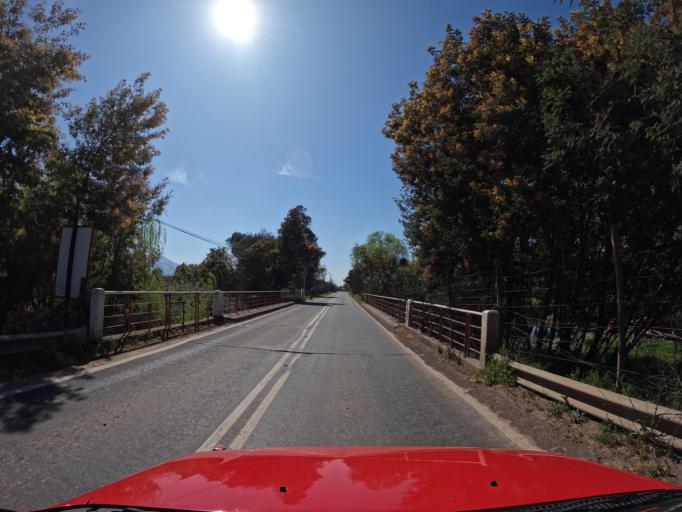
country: CL
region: Maule
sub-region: Provincia de Curico
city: Rauco
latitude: -35.0480
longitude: -71.4670
